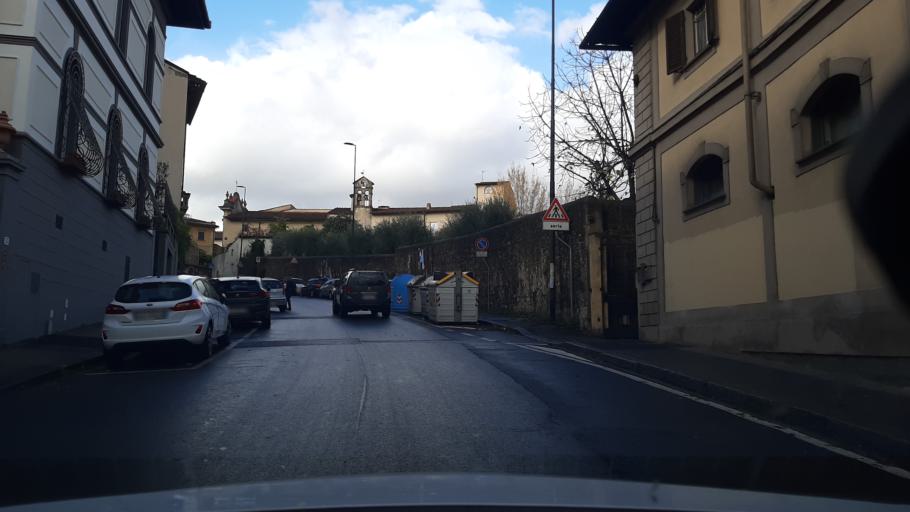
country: IT
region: Tuscany
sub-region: Province of Florence
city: Florence
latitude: 43.7898
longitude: 11.2626
